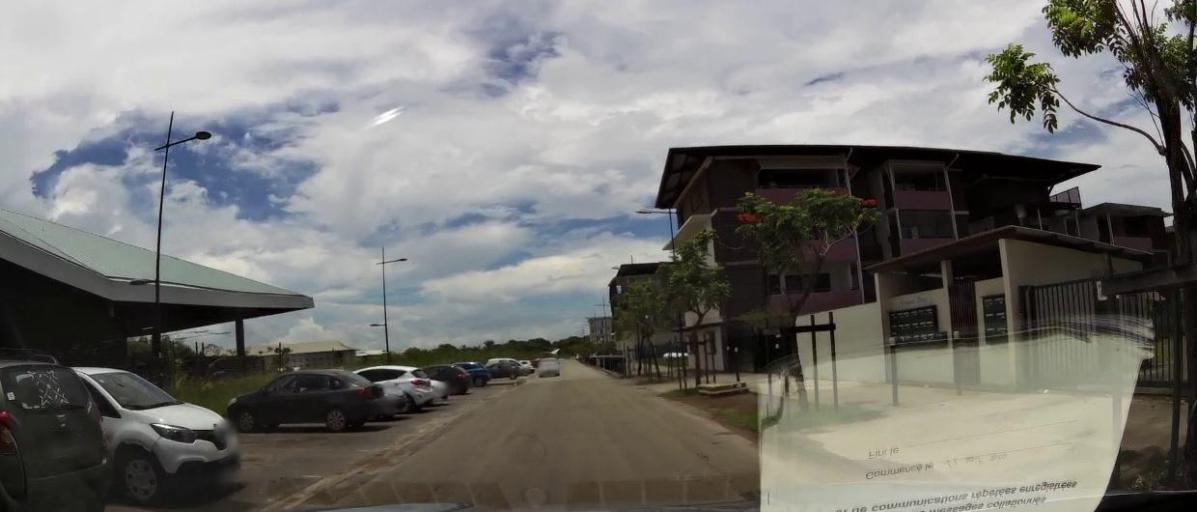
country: GF
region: Guyane
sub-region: Guyane
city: Cayenne
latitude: 4.9337
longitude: -52.3016
